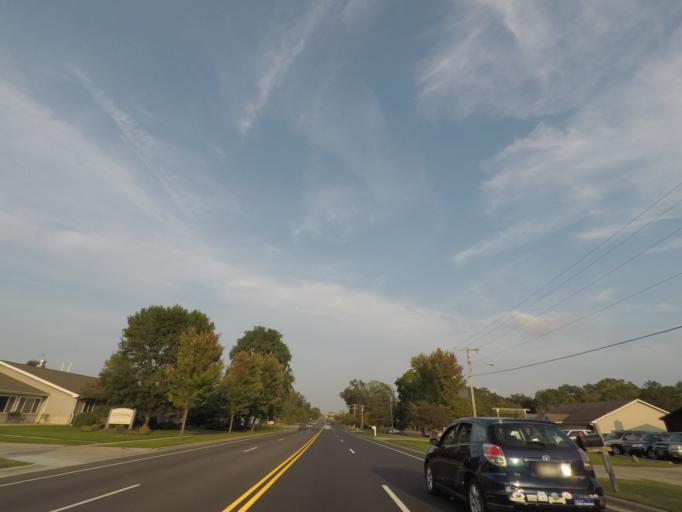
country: US
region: Wisconsin
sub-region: Dane County
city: Cottage Grove
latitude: 43.0866
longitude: -89.2076
